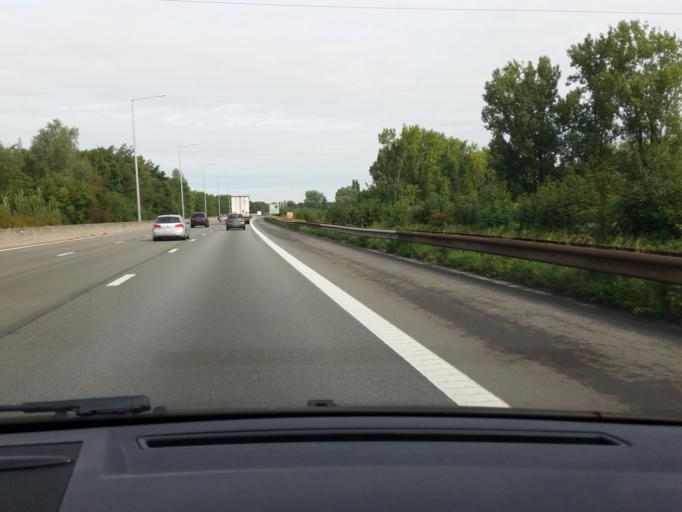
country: BE
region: Flanders
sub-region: Provincie Antwerpen
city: Kontich
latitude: 51.1130
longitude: 4.4313
